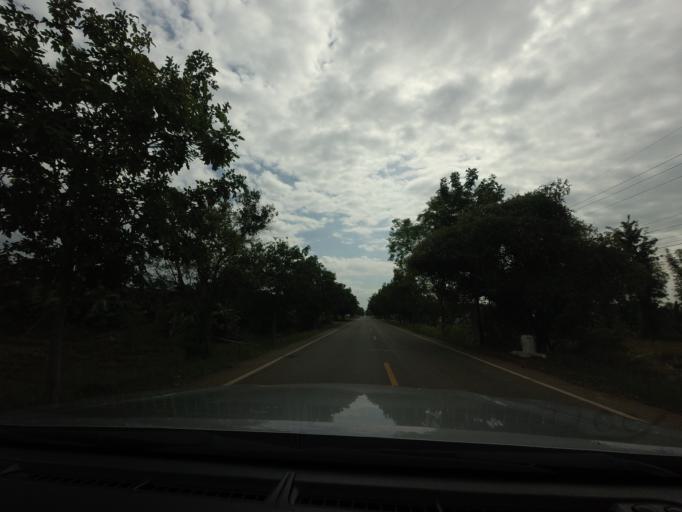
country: TH
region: Phitsanulok
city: Noen Maprang
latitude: 16.6018
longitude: 100.6225
